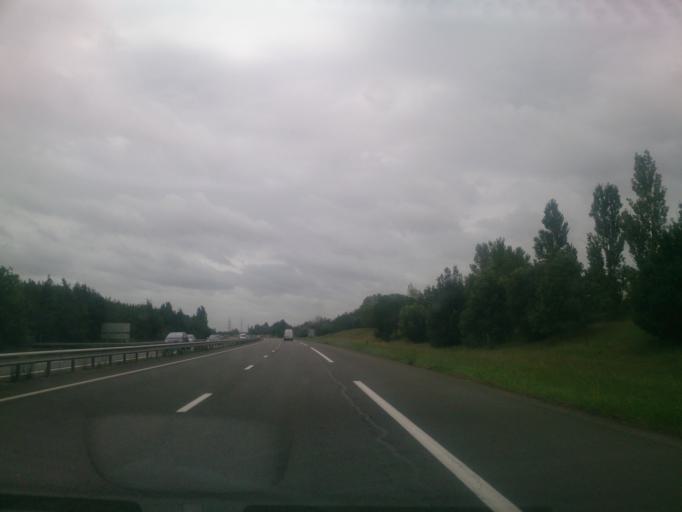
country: FR
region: Midi-Pyrenees
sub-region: Departement de la Haute-Garonne
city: Frouzins
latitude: 43.4939
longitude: 1.3340
